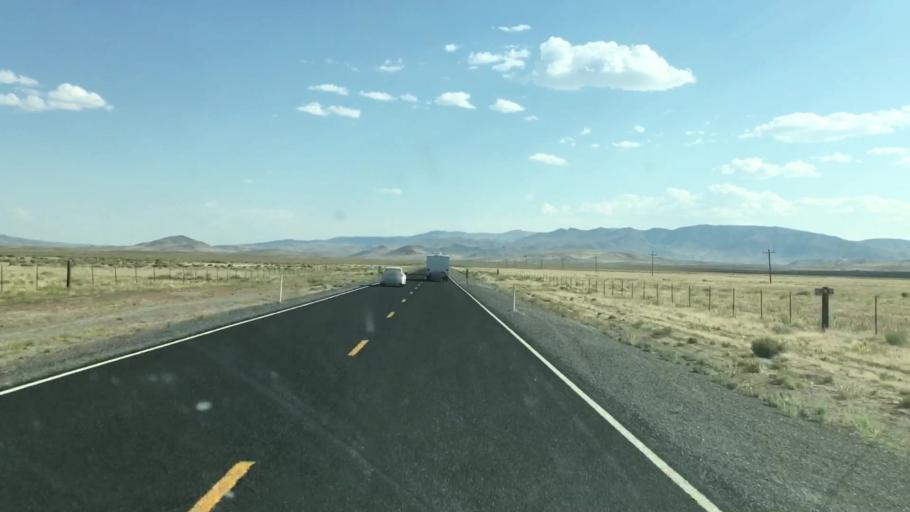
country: US
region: Nevada
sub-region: Lyon County
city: Fernley
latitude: 39.6804
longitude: -119.3344
